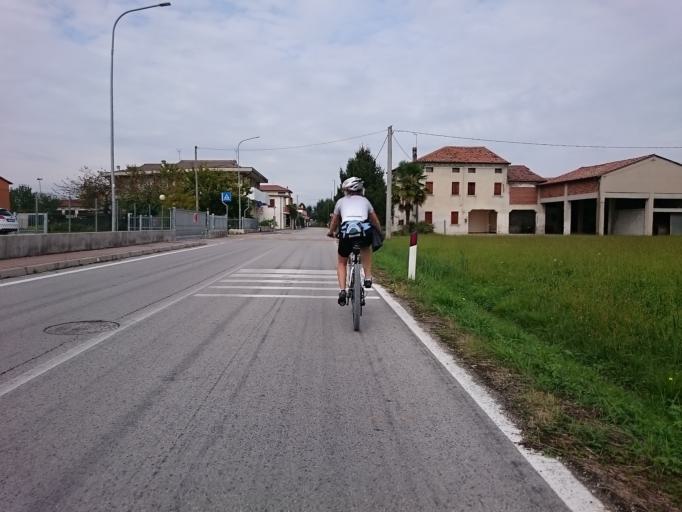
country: IT
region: Veneto
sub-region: Provincia di Padova
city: San Pietro in Gu
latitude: 45.5816
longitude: 11.6638
